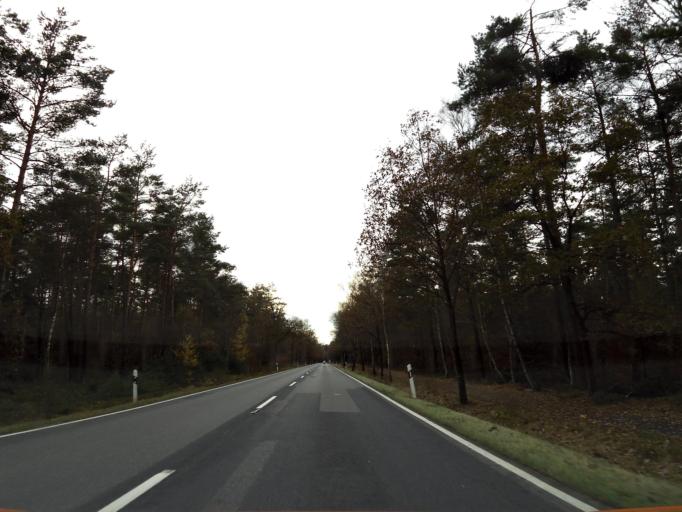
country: DE
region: Lower Saxony
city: Fassberg
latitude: 52.9741
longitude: 10.2095
